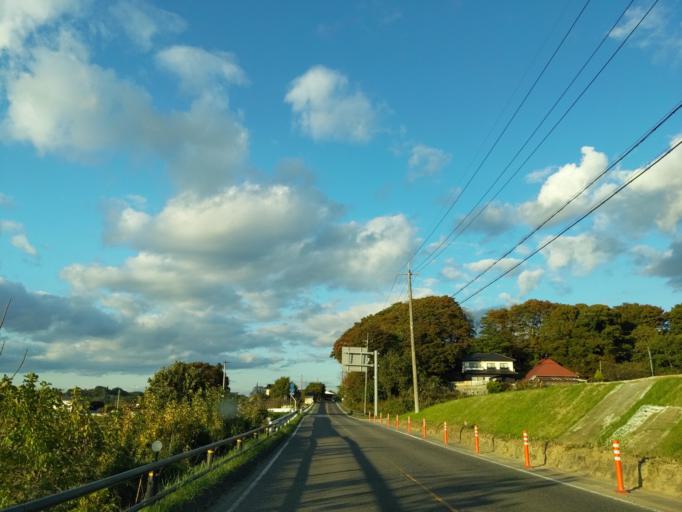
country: JP
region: Fukushima
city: Koriyama
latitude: 37.4293
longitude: 140.4193
